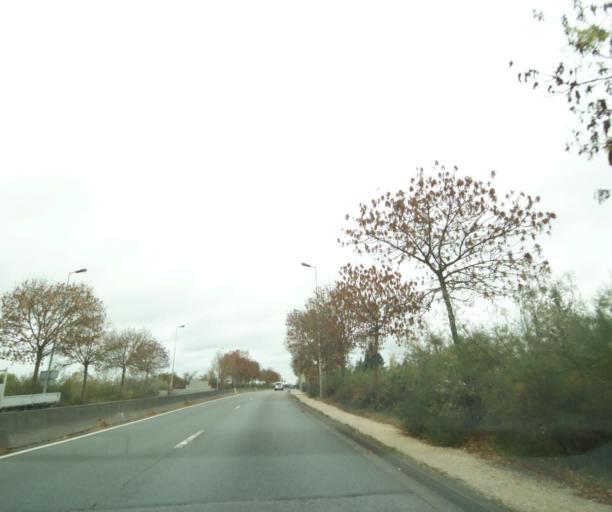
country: FR
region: Centre
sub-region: Departement d'Eure-et-Loir
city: Dreux
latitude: 48.7349
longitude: 1.3421
